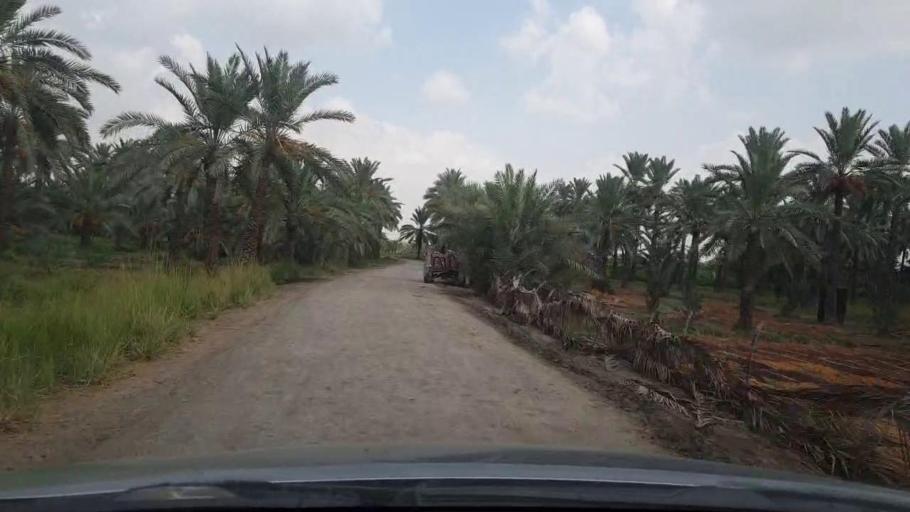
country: PK
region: Sindh
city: Khairpur
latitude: 27.4654
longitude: 68.7568
